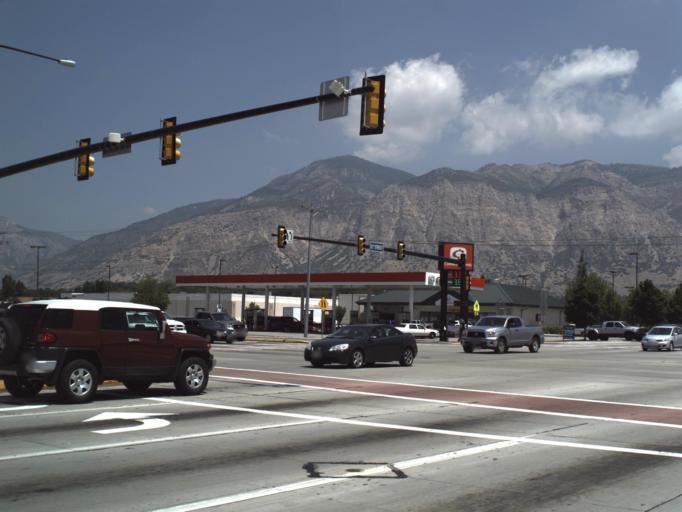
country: US
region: Utah
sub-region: Weber County
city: Ogden
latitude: 41.2442
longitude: -111.9817
